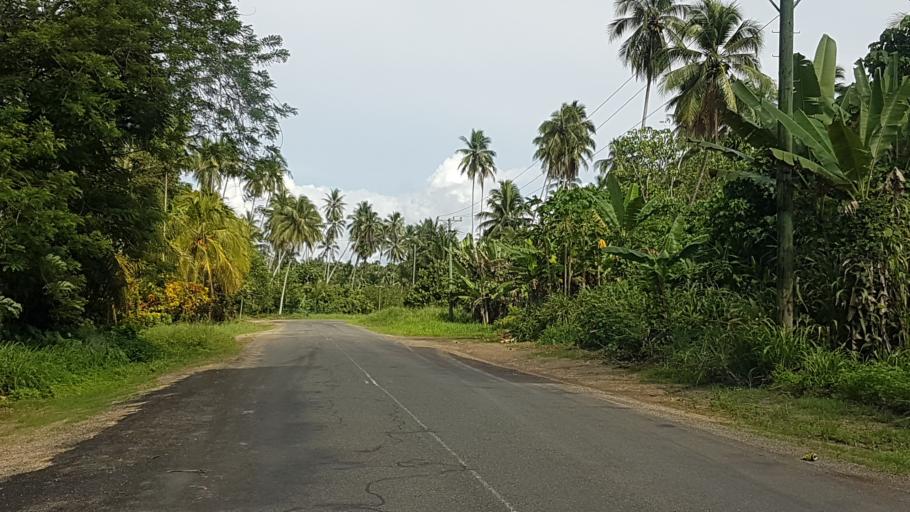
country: PG
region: Madang
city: Madang
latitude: -4.9911
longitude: 145.7897
